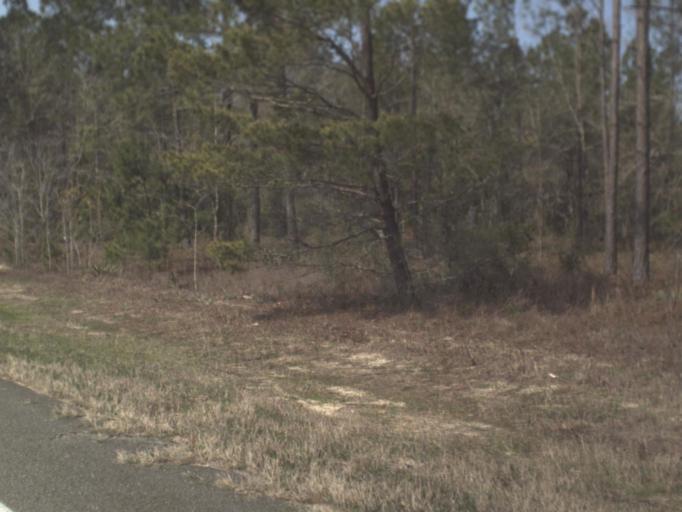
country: US
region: Florida
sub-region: Liberty County
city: Bristol
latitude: 30.5083
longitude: -84.8341
